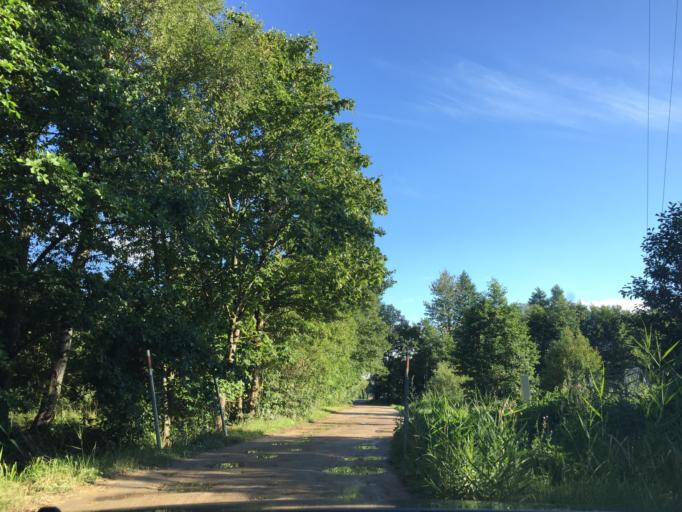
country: LV
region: Riga
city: Jaunciems
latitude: 57.0535
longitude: 24.1316
